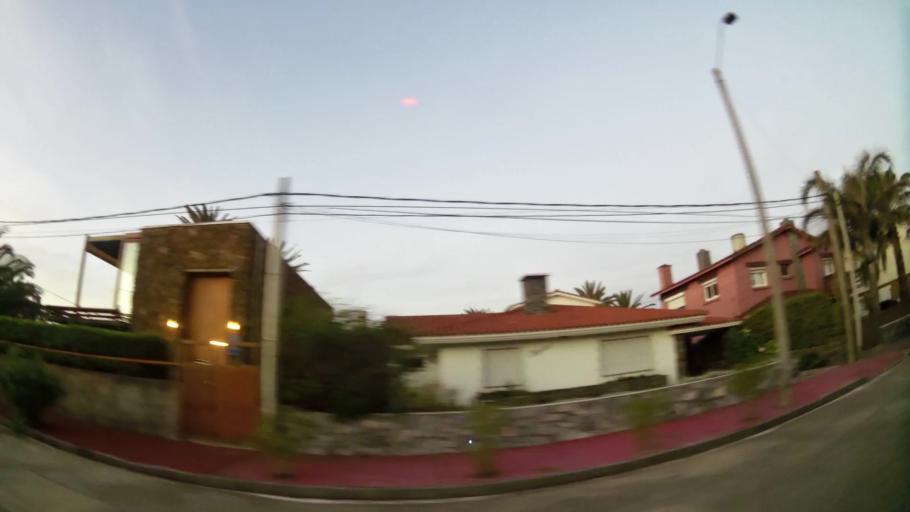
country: UY
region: Maldonado
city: Punta del Este
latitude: -34.9675
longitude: -54.9521
